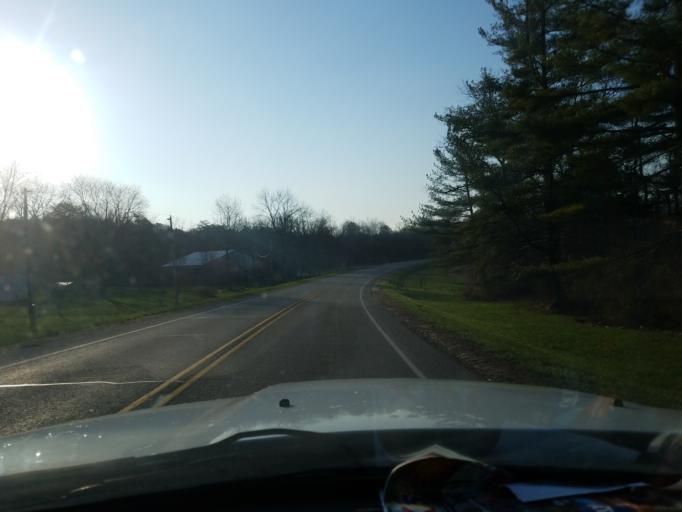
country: US
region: Indiana
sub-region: Vigo County
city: Seelyville
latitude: 39.4071
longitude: -87.3244
